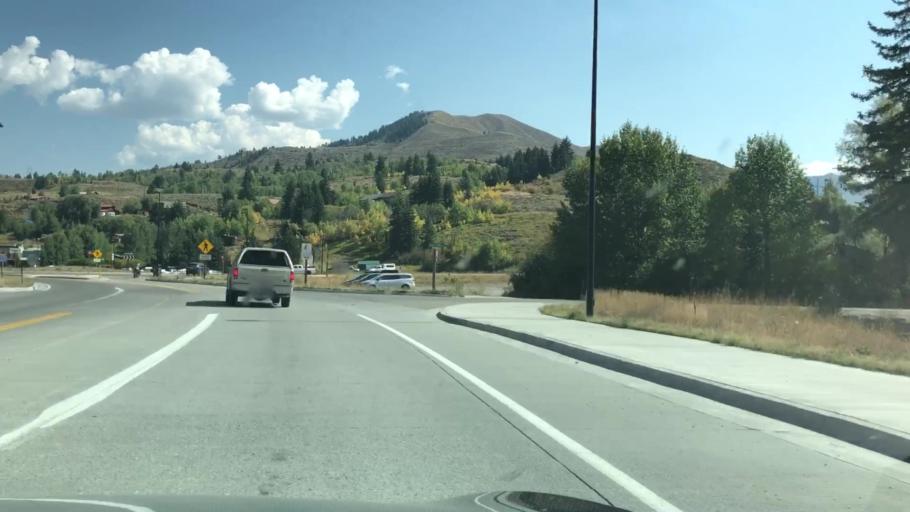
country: US
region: Wyoming
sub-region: Teton County
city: Hoback
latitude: 43.3214
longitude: -110.7317
